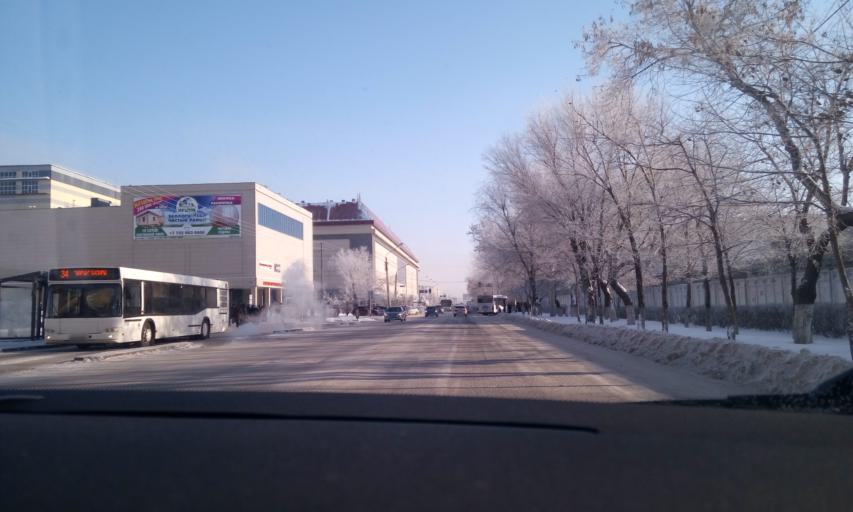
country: KZ
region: Astana Qalasy
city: Astana
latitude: 51.1723
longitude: 71.4334
